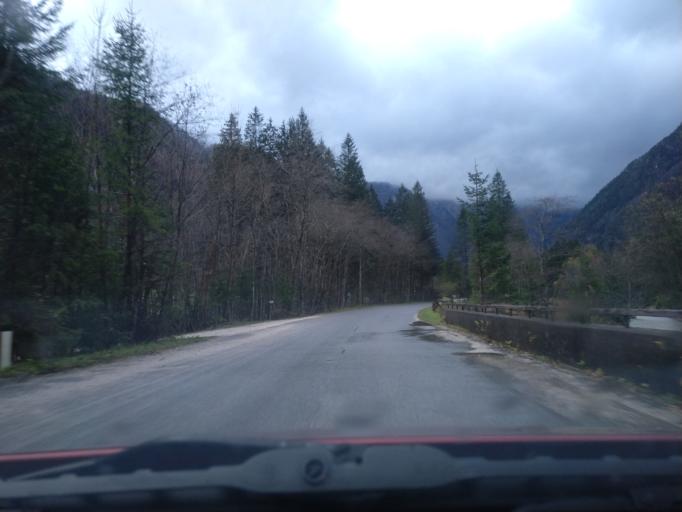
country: SI
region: Solcava
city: Solcava
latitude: 46.4099
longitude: 14.6371
